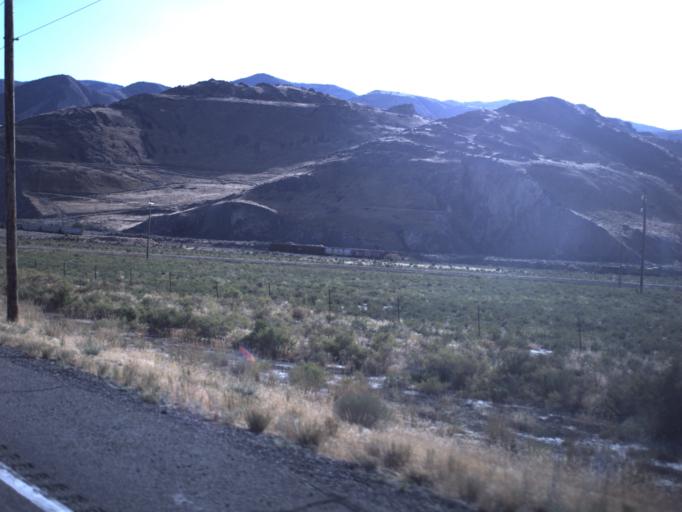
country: US
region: Utah
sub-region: Tooele County
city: Grantsville
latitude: 40.6783
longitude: -112.5503
